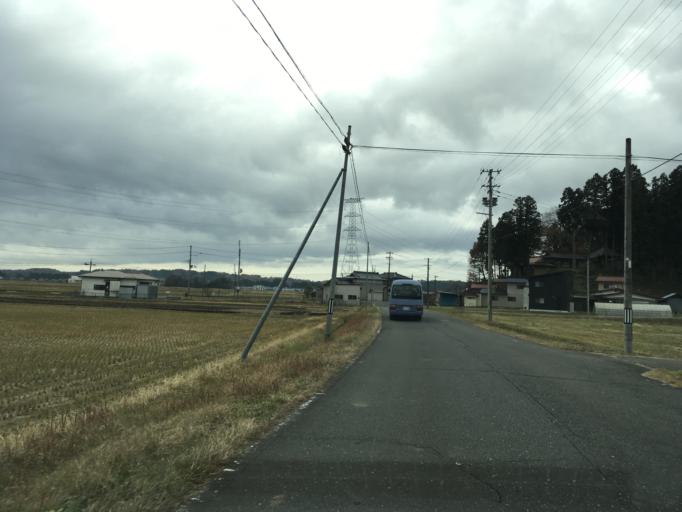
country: JP
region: Iwate
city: Ichinoseki
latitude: 38.8230
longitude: 141.0444
